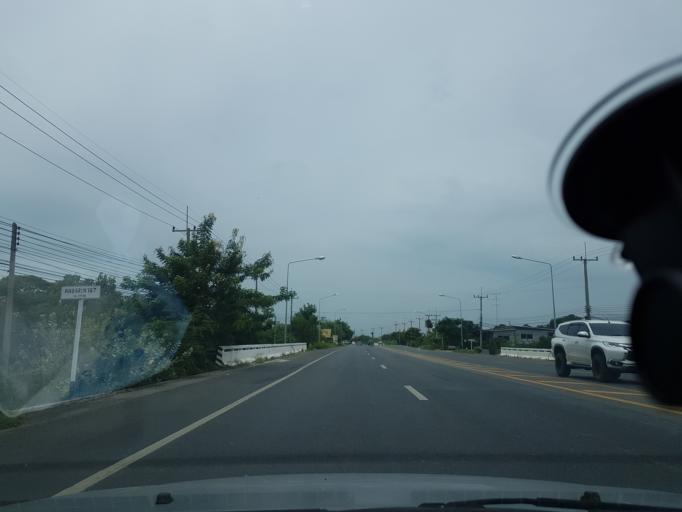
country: TH
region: Lop Buri
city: Lop Buri
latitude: 14.8091
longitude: 100.5883
